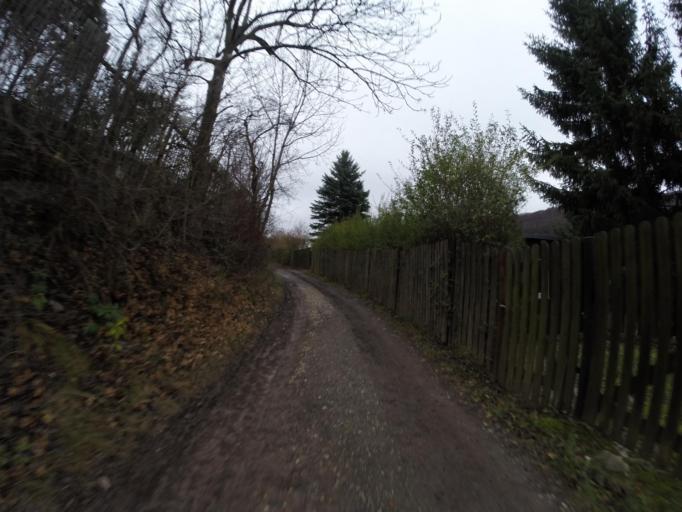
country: DE
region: Thuringia
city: Jena
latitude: 50.9210
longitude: 11.6215
